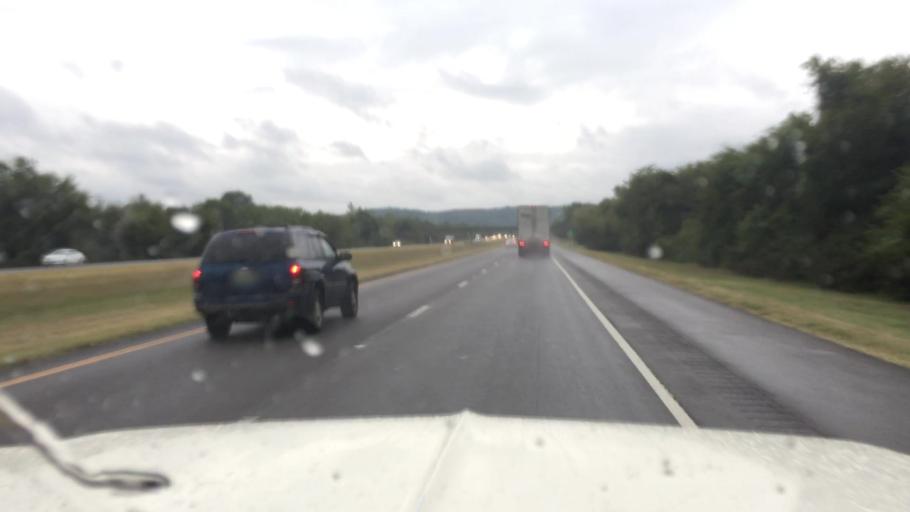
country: US
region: Alabama
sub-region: Morgan County
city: Falkville
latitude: 34.3573
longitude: -86.8919
